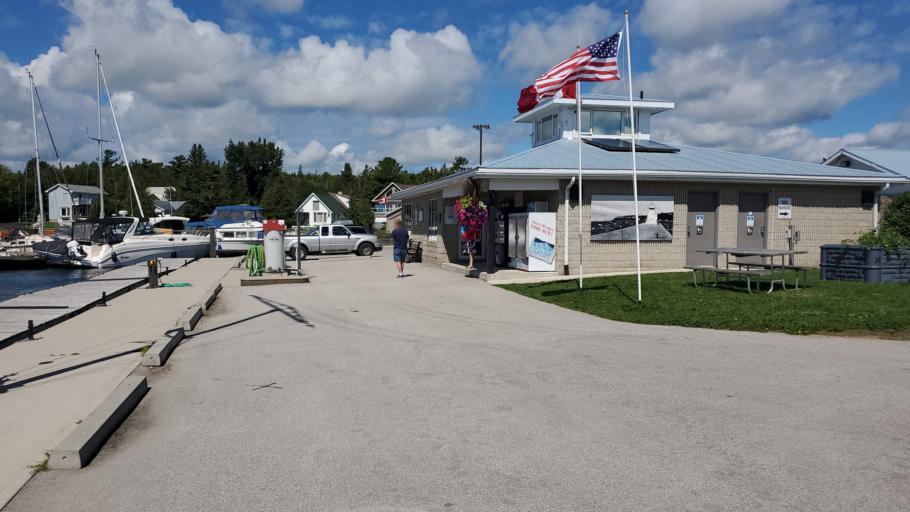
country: CA
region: Ontario
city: Tobermory
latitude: 44.9905
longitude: -81.2493
